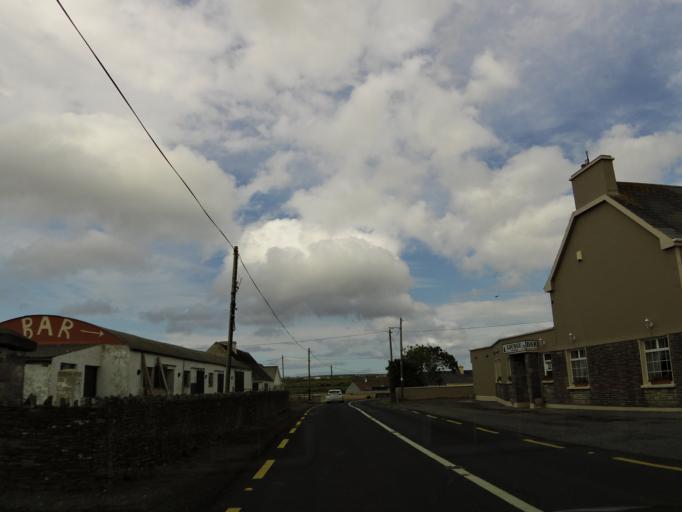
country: IE
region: Munster
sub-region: An Clar
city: Kilrush
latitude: 52.7168
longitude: -9.5889
